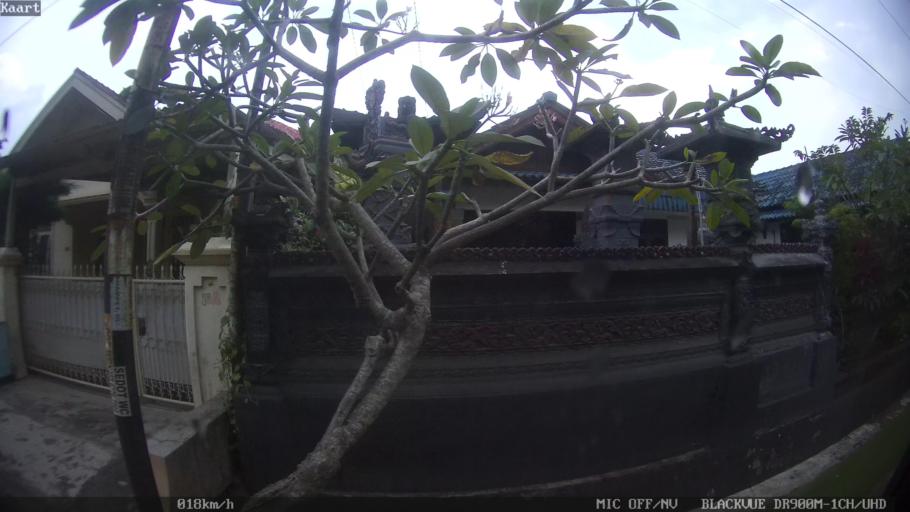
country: ID
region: Lampung
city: Bandarlampung
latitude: -5.4378
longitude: 105.2845
